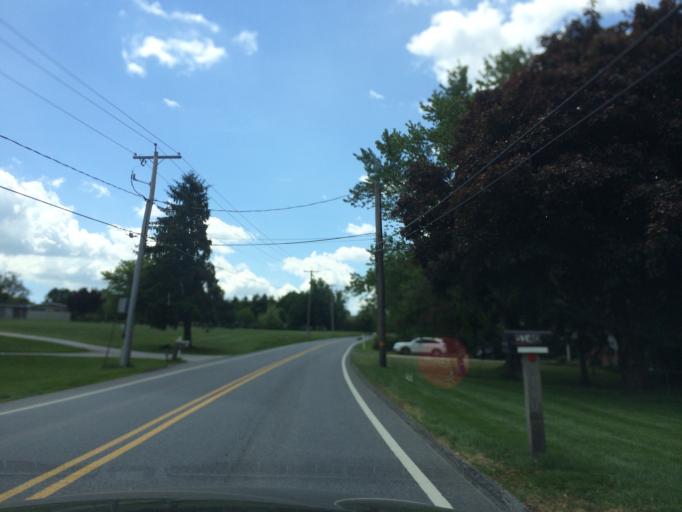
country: US
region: Maryland
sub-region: Carroll County
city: Sykesville
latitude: 39.4335
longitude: -77.0534
